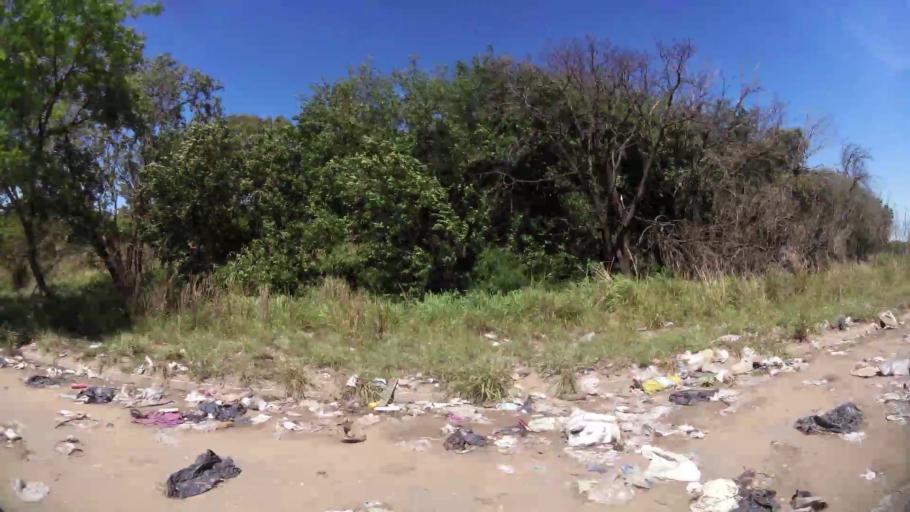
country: AR
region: Cordoba
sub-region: Departamento de Capital
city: Cordoba
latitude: -31.4064
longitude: -64.1330
